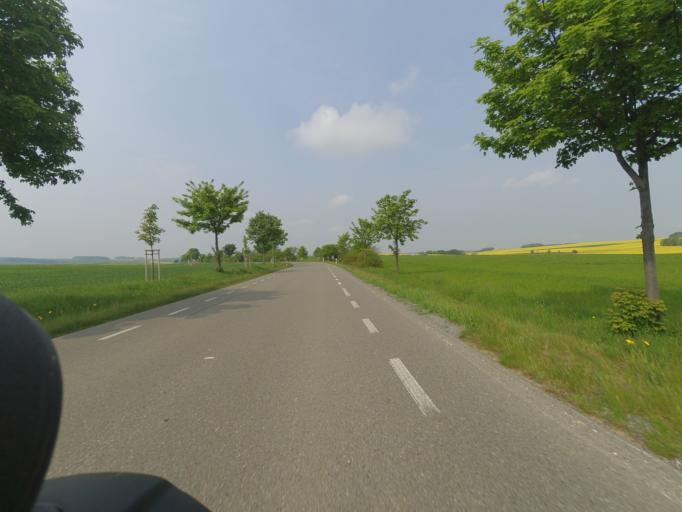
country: DE
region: Saxony
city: Pretzschendorf
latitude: 50.8644
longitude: 13.4924
